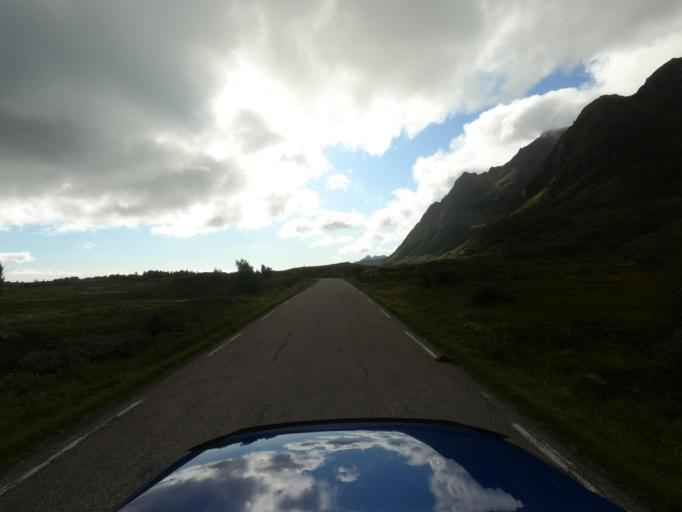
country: NO
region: Nordland
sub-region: Vestvagoy
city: Evjen
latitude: 68.1875
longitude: 13.8590
